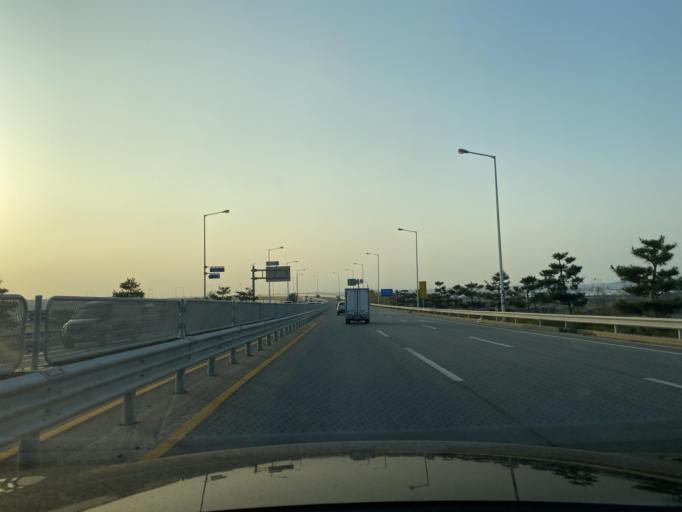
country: KR
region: Chungcheongnam-do
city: Yesan
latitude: 36.7042
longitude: 126.8286
